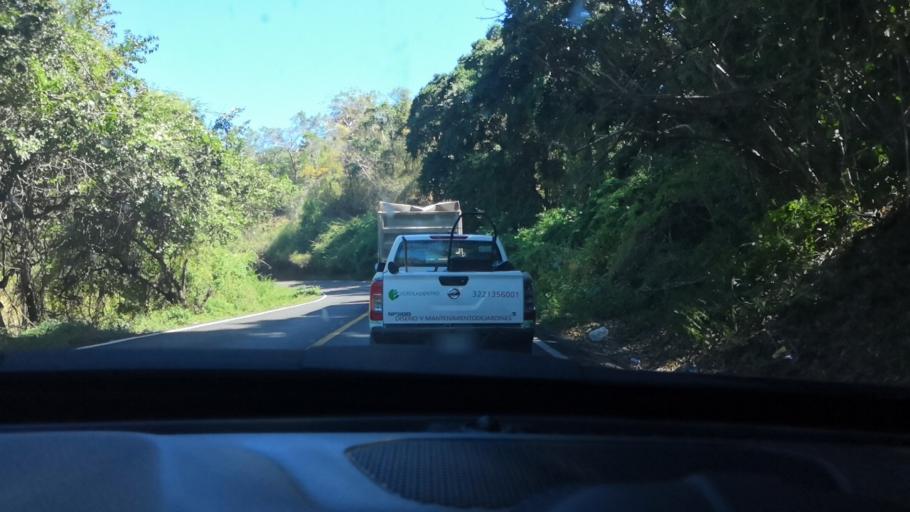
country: MX
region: Nayarit
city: Bucerias
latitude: 20.8024
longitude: -105.3860
